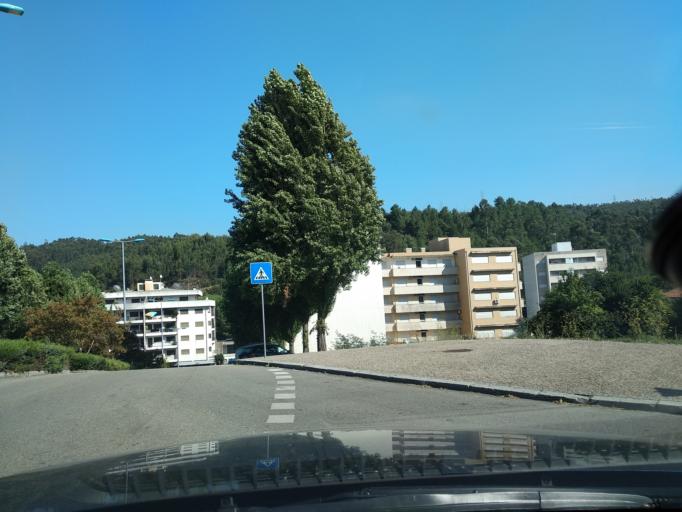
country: PT
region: Porto
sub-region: Paredes
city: Rebordosa
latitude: 41.2201
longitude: -8.4120
